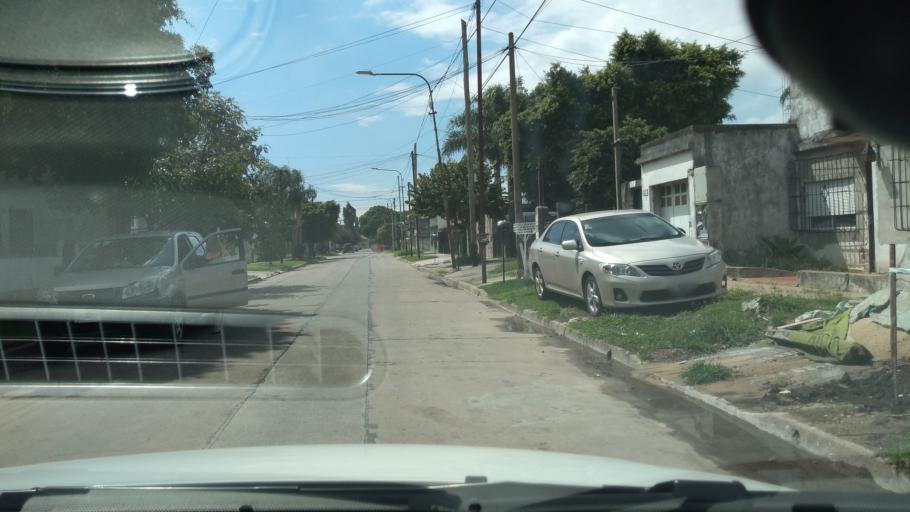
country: AR
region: Buenos Aires
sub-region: Partido de Moron
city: Moron
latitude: -34.6657
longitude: -58.6053
